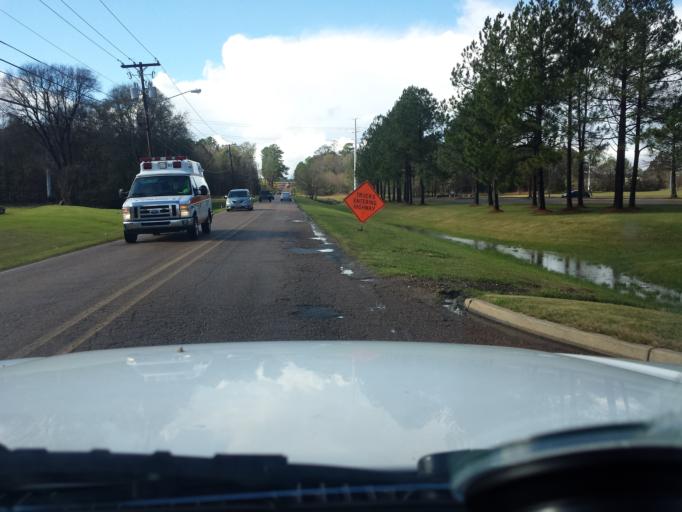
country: US
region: Mississippi
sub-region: Madison County
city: Madison
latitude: 32.4579
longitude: -90.1282
